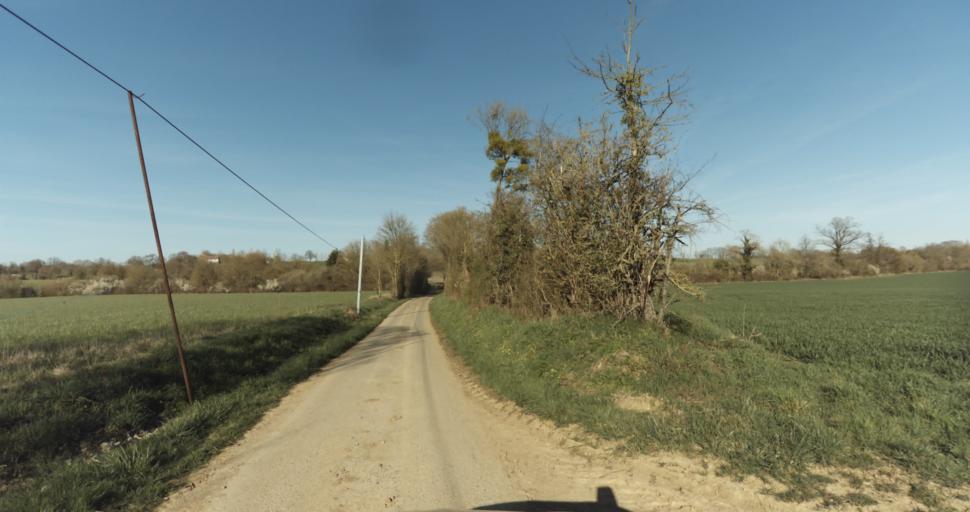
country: FR
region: Lower Normandy
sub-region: Departement du Calvados
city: Livarot
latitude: 49.0542
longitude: 0.0736
